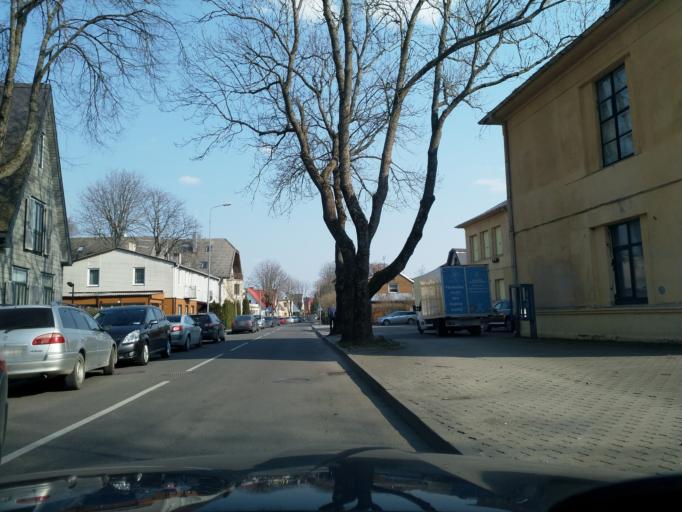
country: LT
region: Klaipedos apskritis
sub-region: Klaipeda
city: Palanga
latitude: 55.9134
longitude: 21.0643
